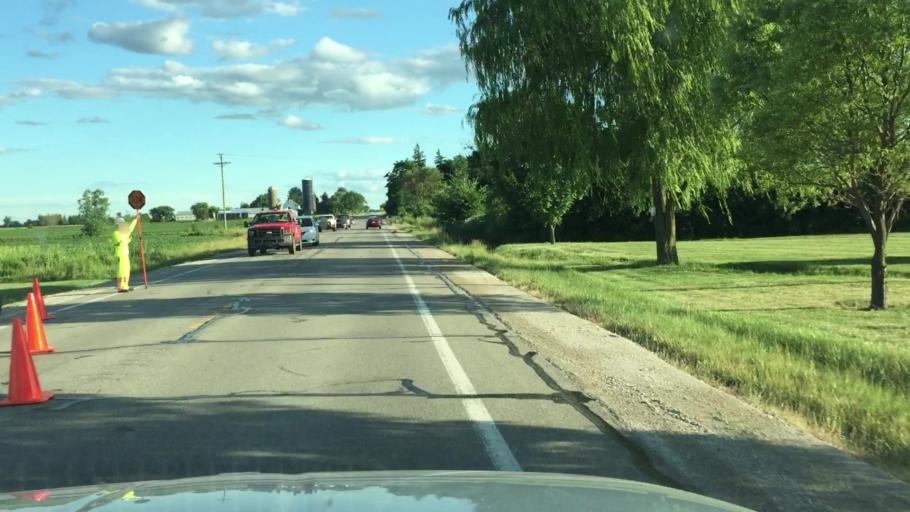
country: US
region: Michigan
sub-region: Saint Clair County
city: Yale
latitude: 43.0951
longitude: -82.7665
